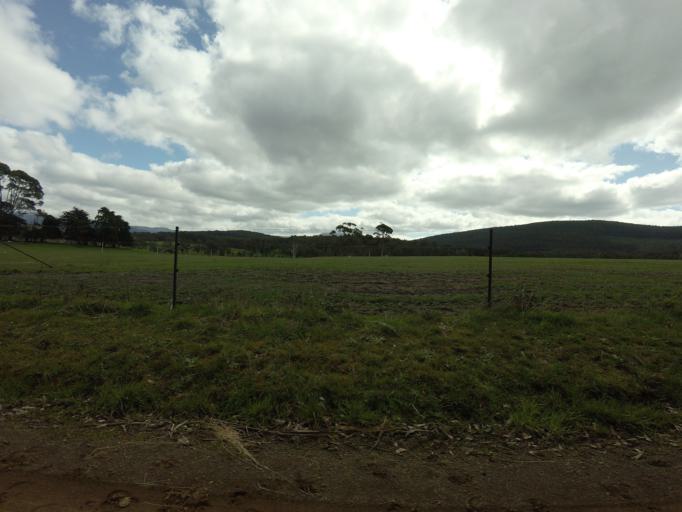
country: AU
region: Tasmania
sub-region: Huon Valley
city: Geeveston
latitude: -43.4314
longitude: 146.9902
